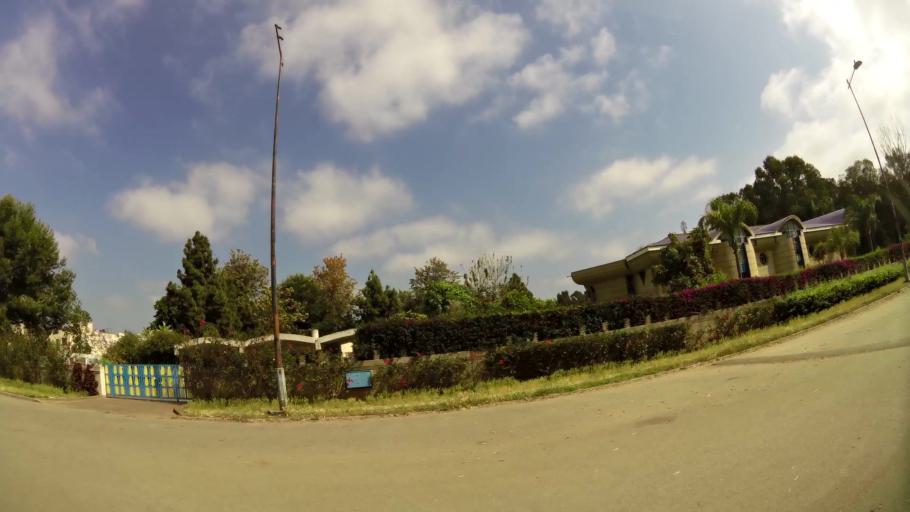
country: MA
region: Rabat-Sale-Zemmour-Zaer
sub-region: Rabat
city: Rabat
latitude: 33.9859
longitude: -6.8403
